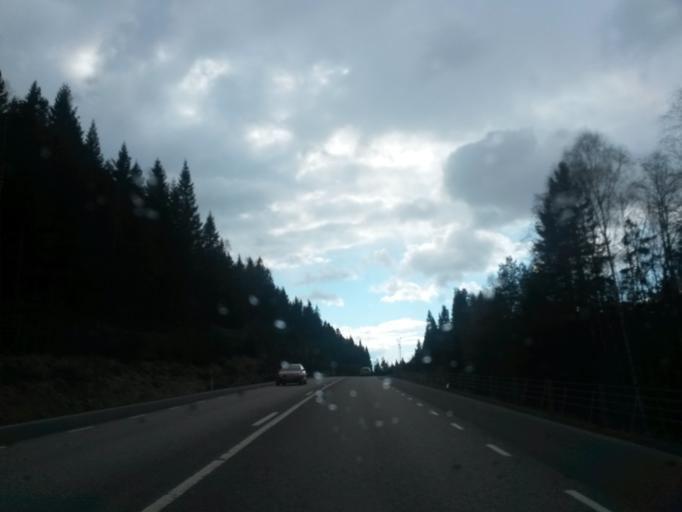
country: SE
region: Vaestra Goetaland
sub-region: Skovde Kommun
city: Skultorp
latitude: 58.3885
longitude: 13.7505
